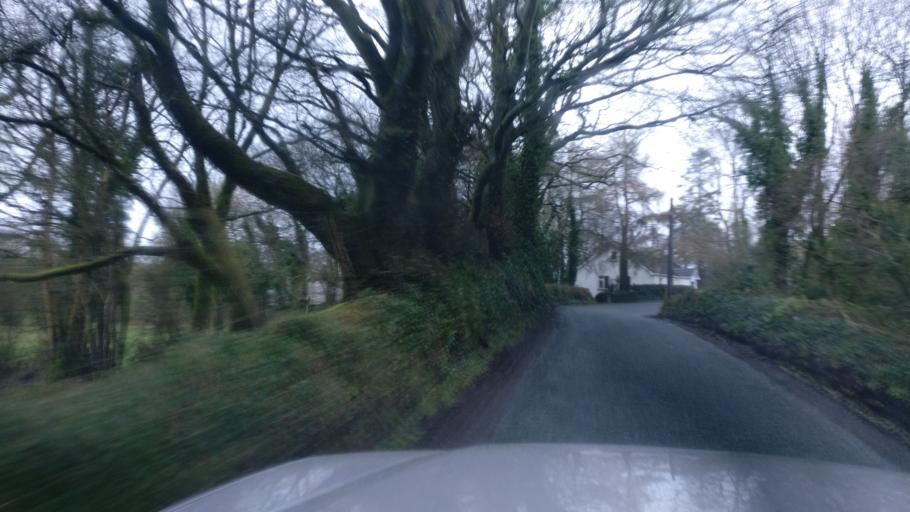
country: IE
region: Connaught
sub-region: County Galway
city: Ballinasloe
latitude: 53.2993
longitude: -8.2700
